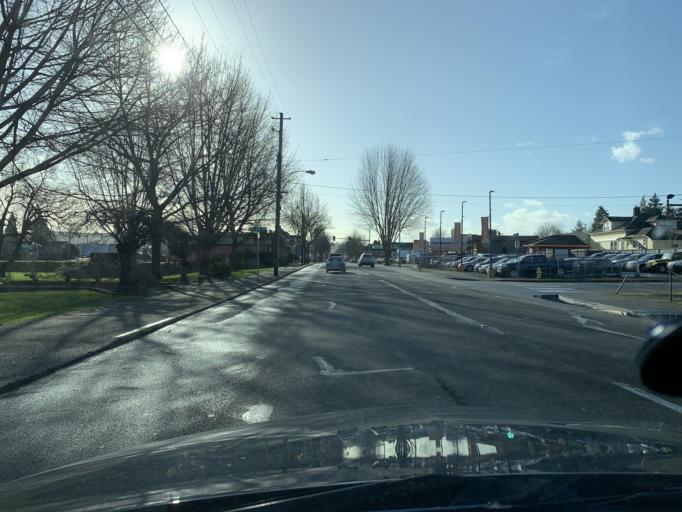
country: US
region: Washington
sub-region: Pierce County
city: Puyallup
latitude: 47.1966
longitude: -122.2937
